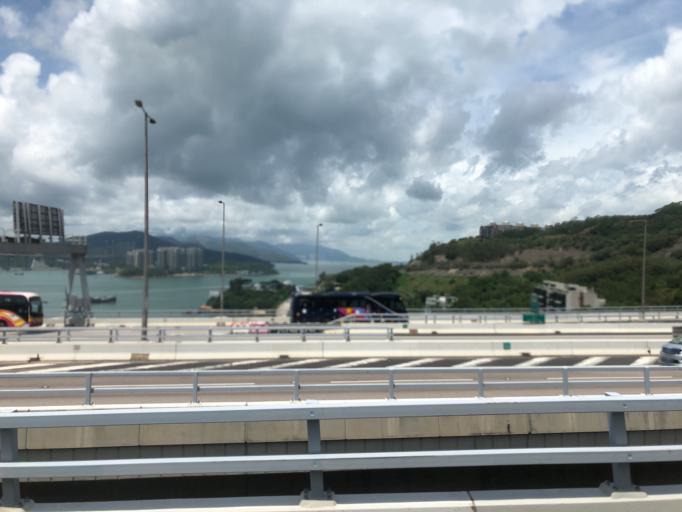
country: HK
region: Tsuen Wan
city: Tsuen Wan
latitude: 22.3695
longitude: 114.0771
